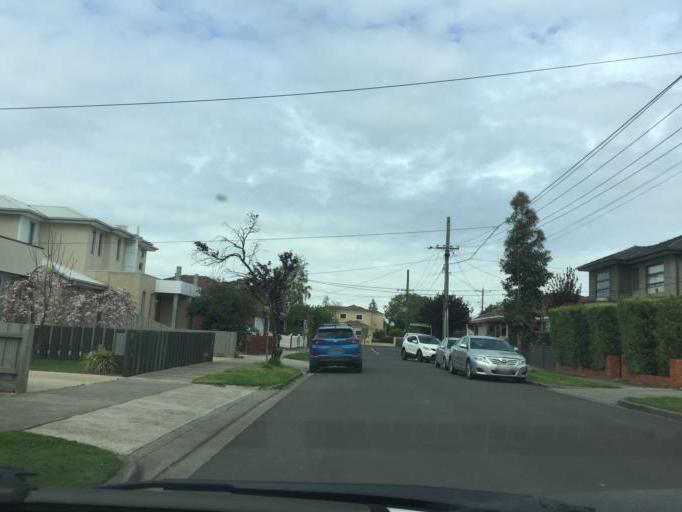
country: AU
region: Victoria
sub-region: Hobsons Bay
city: South Kingsville
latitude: -37.8257
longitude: 144.8747
